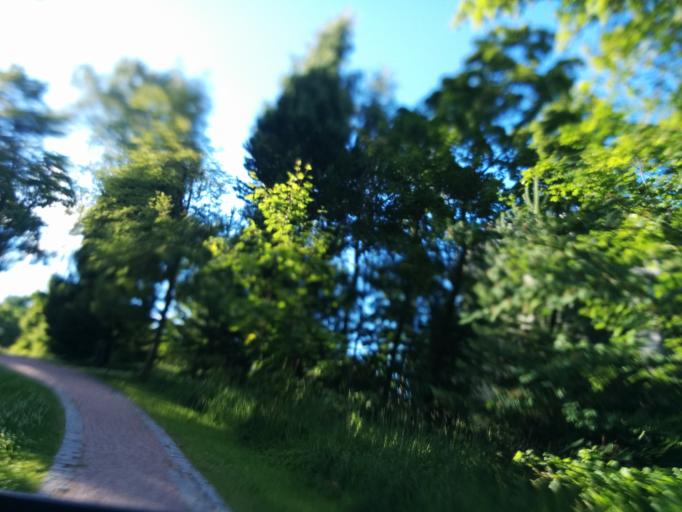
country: FI
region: Uusimaa
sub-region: Helsinki
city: Helsinki
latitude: 60.2062
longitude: 24.9750
